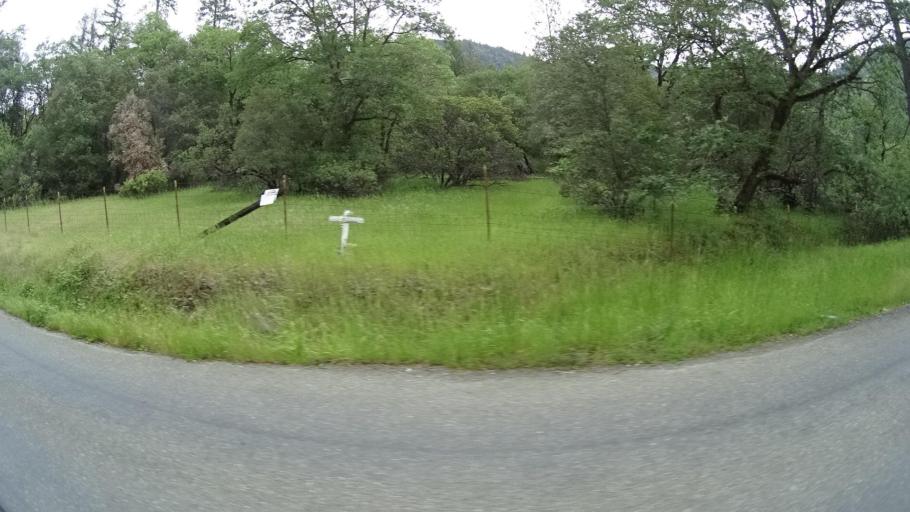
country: US
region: California
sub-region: Humboldt County
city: Willow Creek
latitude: 40.9466
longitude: -123.6251
